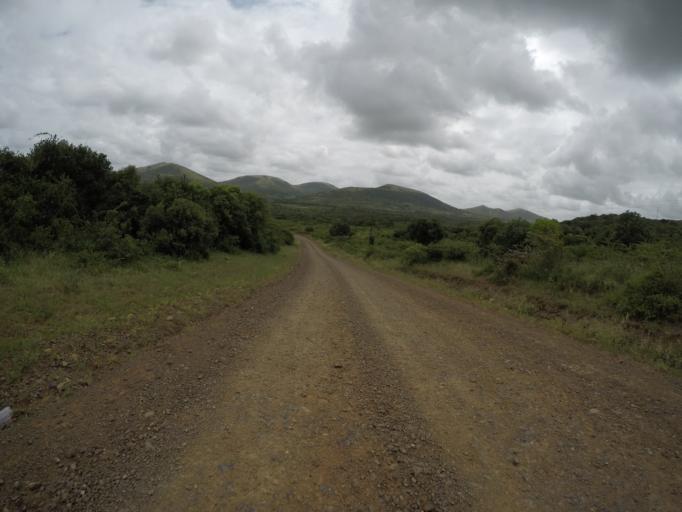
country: ZA
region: KwaZulu-Natal
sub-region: uThungulu District Municipality
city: Empangeni
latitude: -28.6003
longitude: 31.8936
